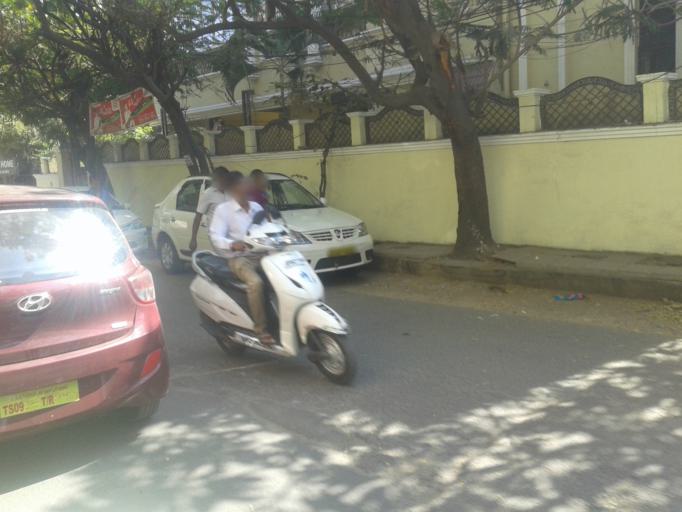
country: IN
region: Telangana
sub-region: Hyderabad
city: Hyderabad
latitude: 17.4072
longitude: 78.4817
